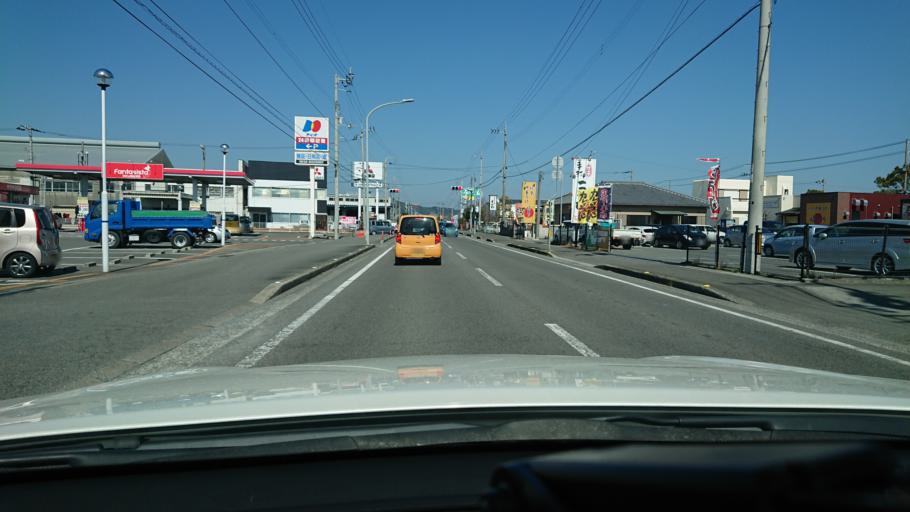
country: JP
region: Tokushima
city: Narutocho-mitsuishi
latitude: 34.1461
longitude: 134.5935
